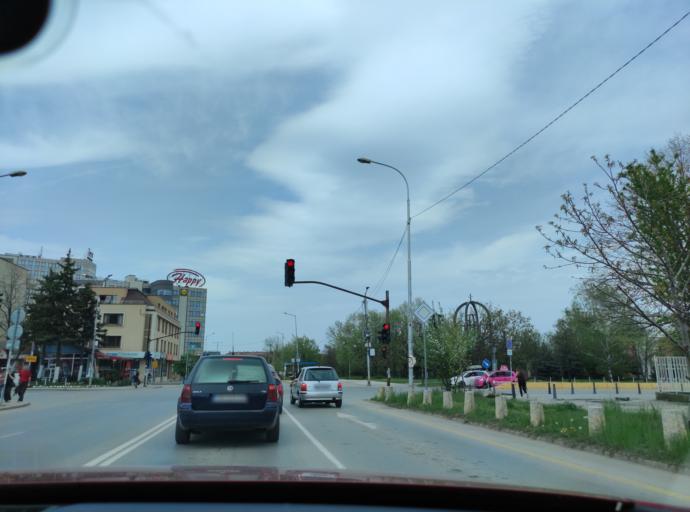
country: BG
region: Sofia-Capital
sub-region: Stolichna Obshtina
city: Sofia
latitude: 42.6516
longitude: 23.3473
